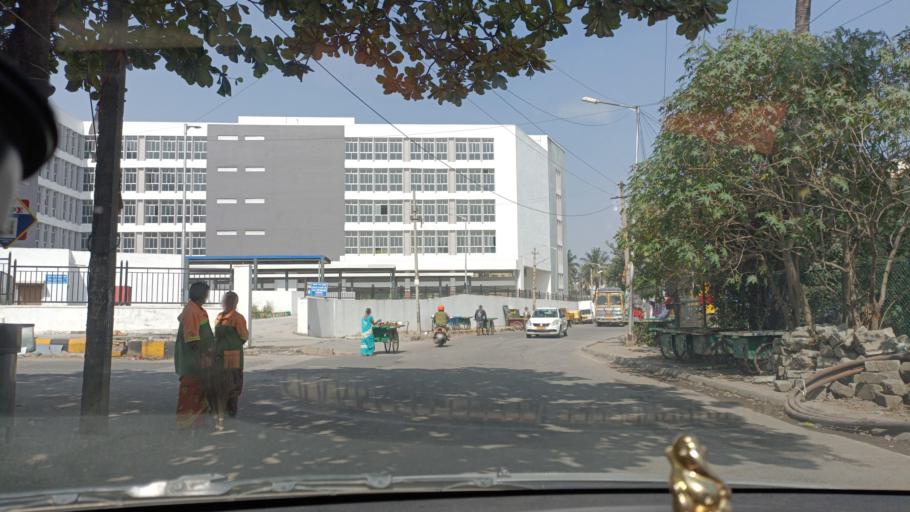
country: IN
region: Karnataka
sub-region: Bangalore Urban
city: Bangalore
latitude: 12.9149
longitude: 77.6163
